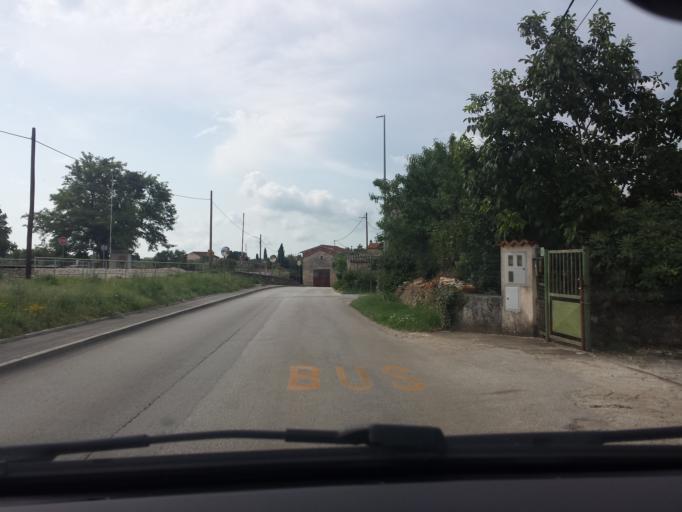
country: HR
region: Istarska
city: Galizana
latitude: 44.9366
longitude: 13.8697
